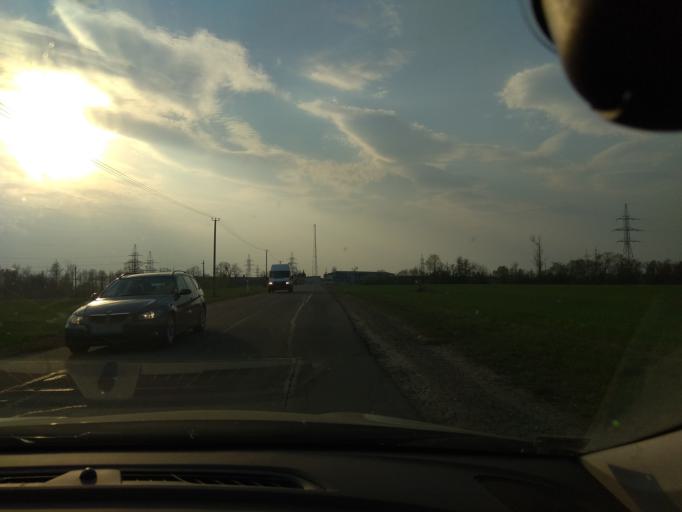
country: LT
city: Baltoji Voke
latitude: 54.6104
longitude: 25.1246
